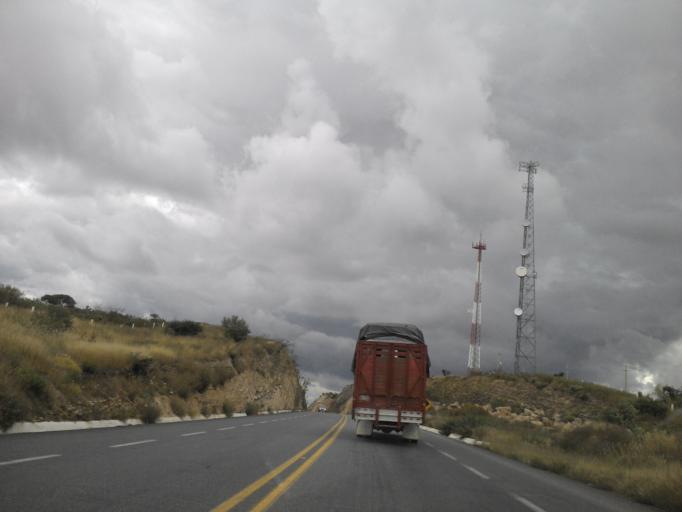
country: MX
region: Zacatecas
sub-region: Rio Grande
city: Las Esperanzas (El Ranchito)
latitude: 23.9136
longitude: -103.1523
